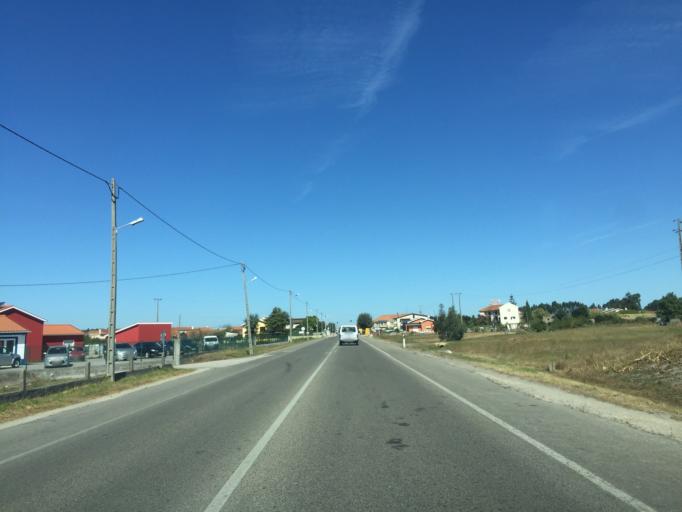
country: PT
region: Coimbra
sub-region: Montemor-O-Velho
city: Arazede
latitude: 40.3037
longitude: -8.7587
